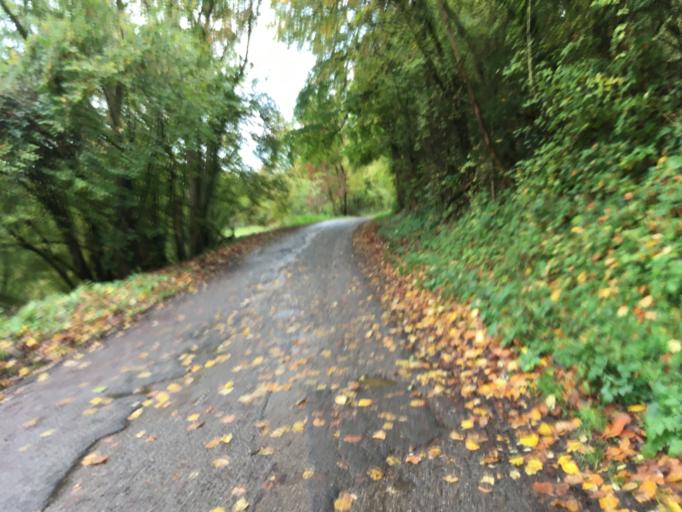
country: DE
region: Baden-Wuerttemberg
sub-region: Regierungsbezirk Stuttgart
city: Widdern
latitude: 49.3120
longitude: 9.4111
